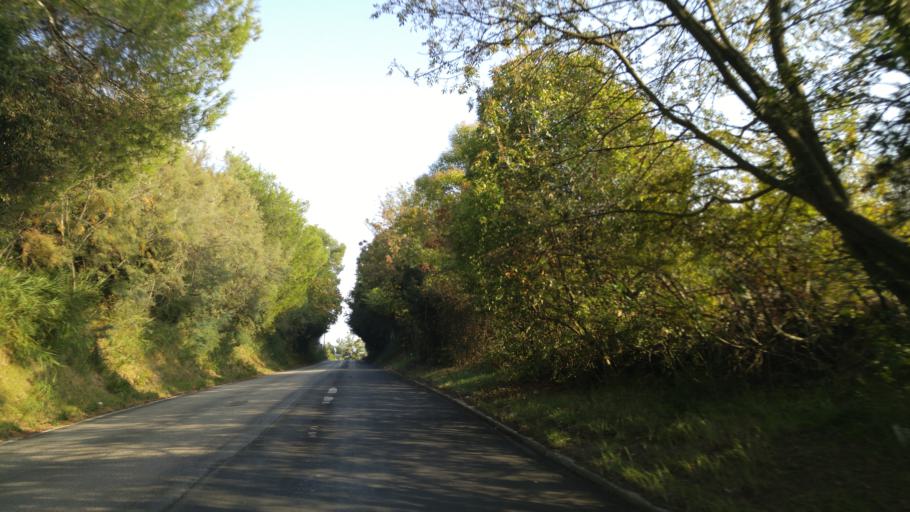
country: IT
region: The Marches
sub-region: Provincia di Pesaro e Urbino
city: Pesaro
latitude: 43.8912
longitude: 12.9457
